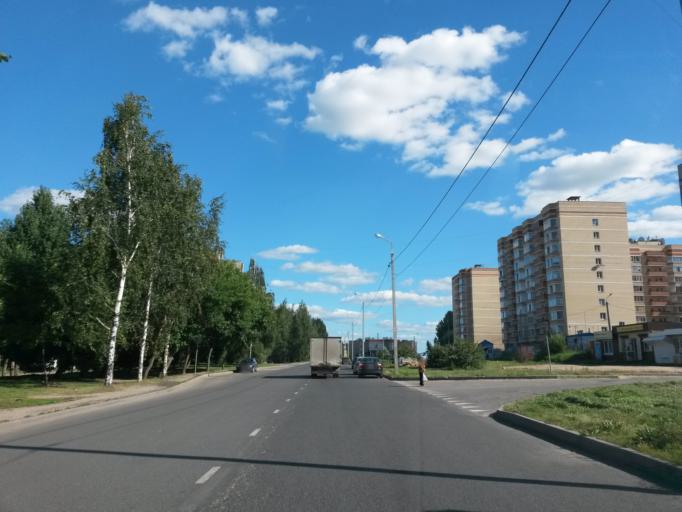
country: RU
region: Jaroslavl
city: Yaroslavl
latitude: 57.5811
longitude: 39.8538
